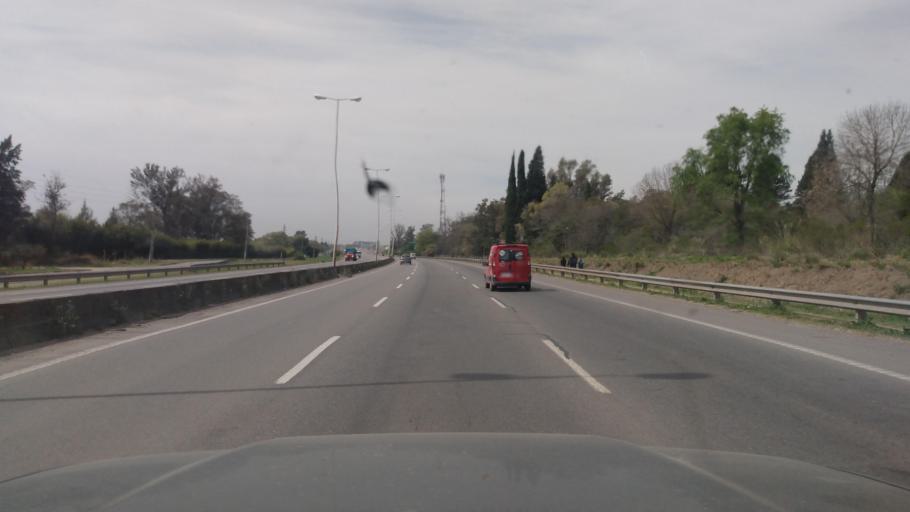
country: AR
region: Buenos Aires
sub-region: Partido de Pilar
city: Pilar
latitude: -34.4375
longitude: -58.9826
